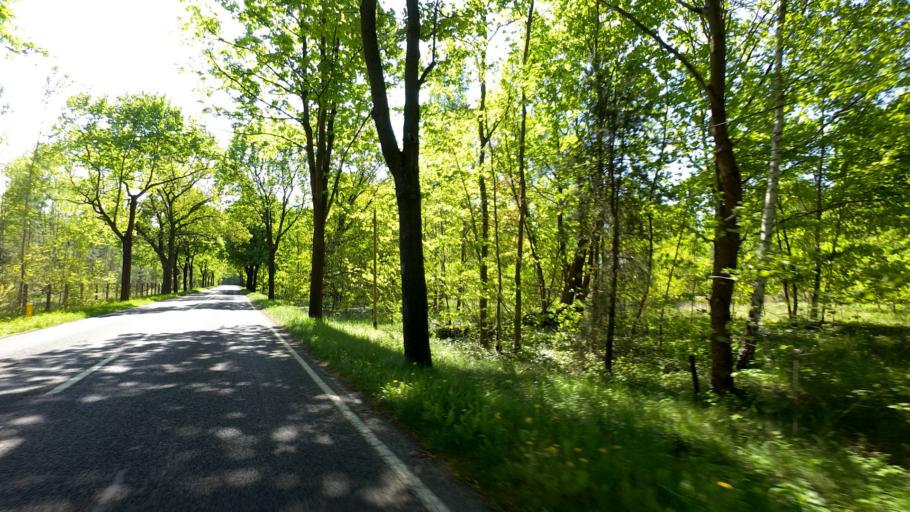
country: DE
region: Brandenburg
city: Bestensee
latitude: 52.2319
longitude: 13.6685
